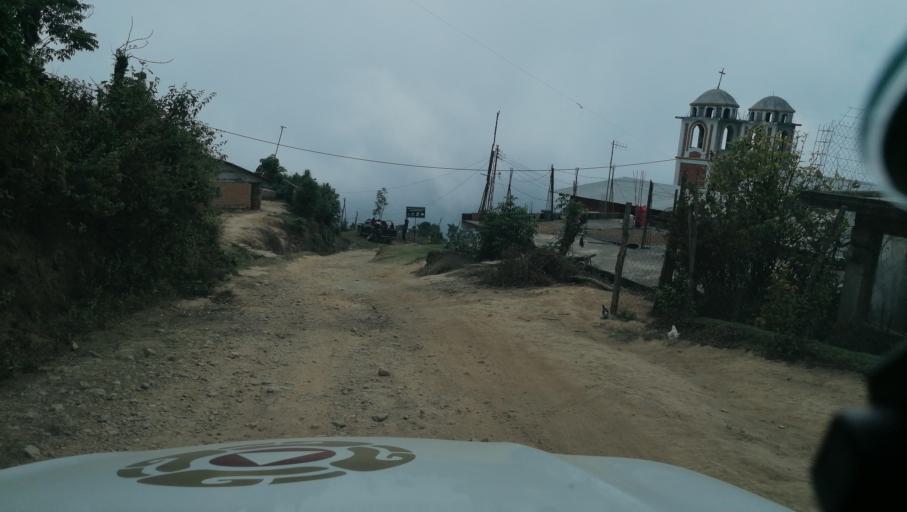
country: GT
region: San Marcos
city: Tacana
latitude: 15.2192
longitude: -92.1899
